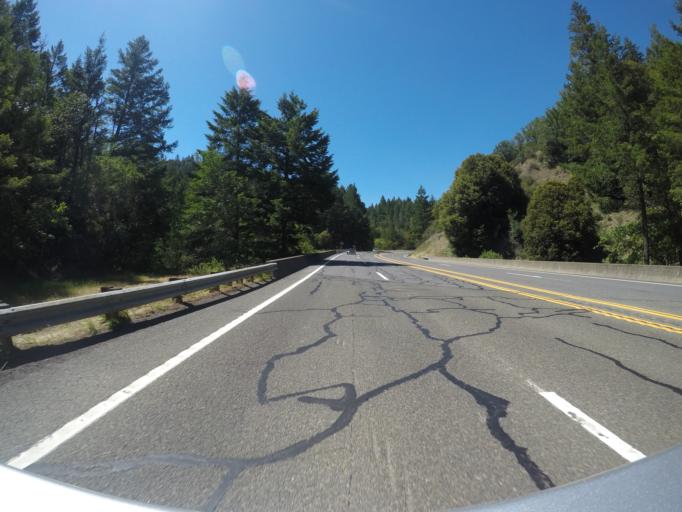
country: US
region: California
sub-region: Mendocino County
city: Laytonville
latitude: 39.6090
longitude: -123.4578
